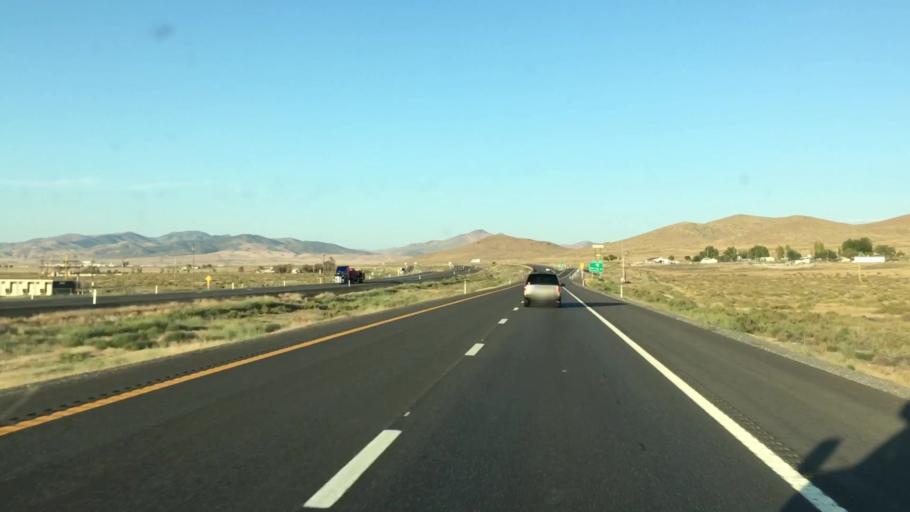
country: US
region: Nevada
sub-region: Humboldt County
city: Winnemucca
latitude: 40.6764
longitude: -118.0766
